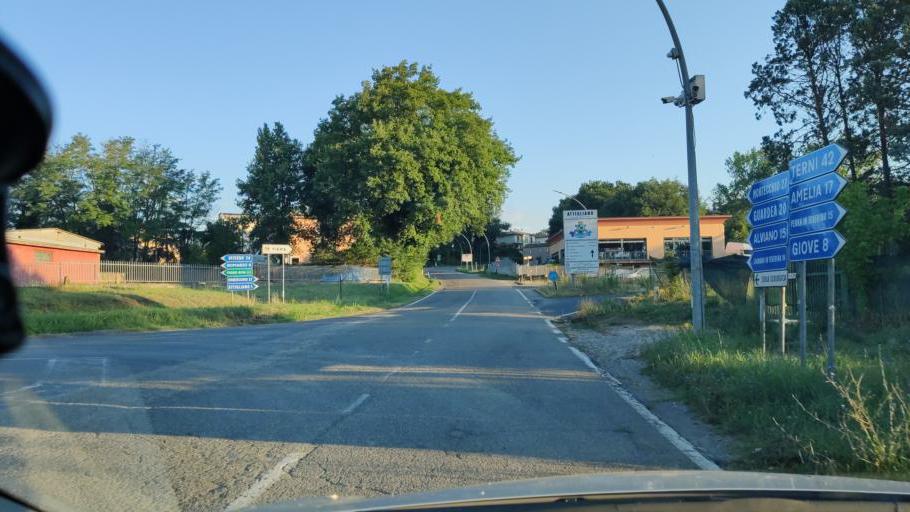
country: IT
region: Umbria
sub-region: Provincia di Terni
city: Attigliano
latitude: 42.5107
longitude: 12.2996
